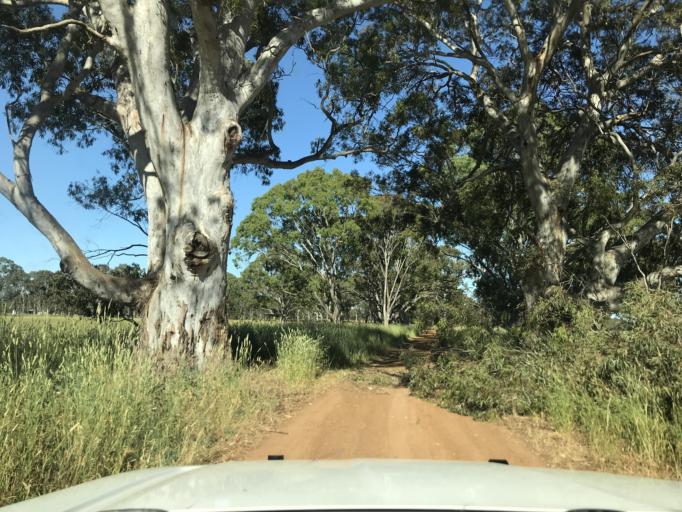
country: AU
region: South Australia
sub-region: Wattle Range
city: Penola
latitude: -37.0840
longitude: 141.3656
